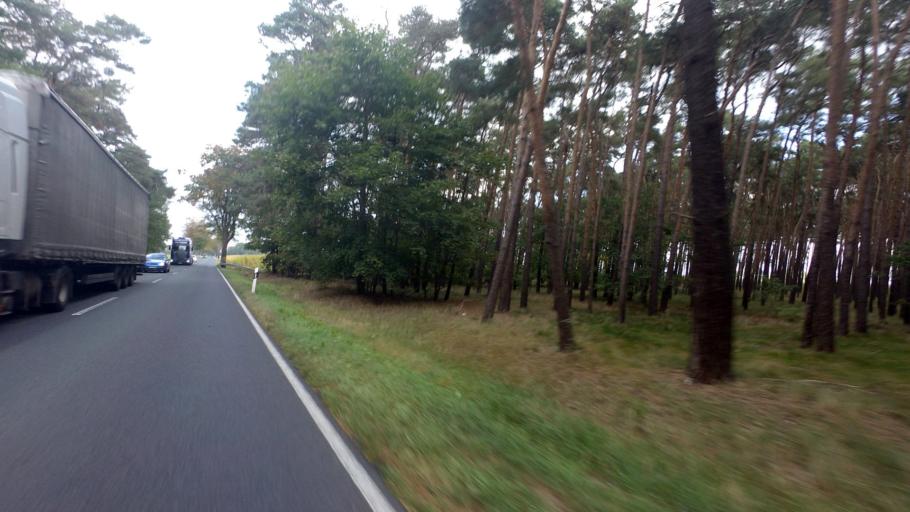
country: DE
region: Saxony-Anhalt
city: Holzdorf
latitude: 51.8061
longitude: 13.1716
